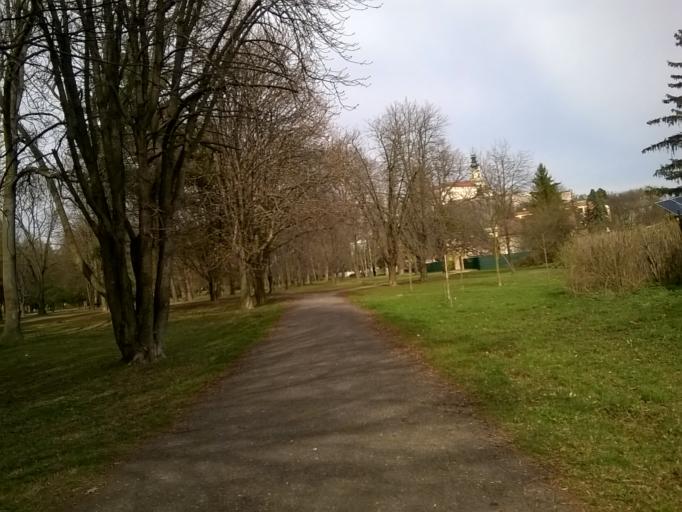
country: SK
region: Nitriansky
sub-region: Okres Nitra
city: Nitra
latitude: 48.3155
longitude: 18.0811
